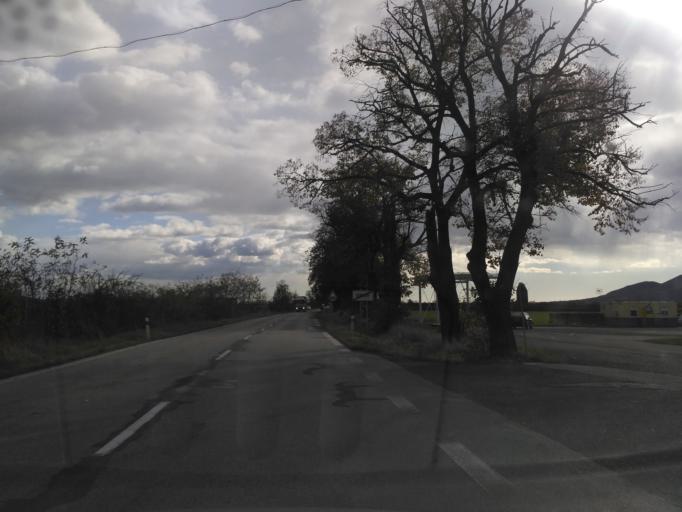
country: HU
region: Borsod-Abauj-Zemplen
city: Satoraljaujhely
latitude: 48.4586
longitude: 21.6442
